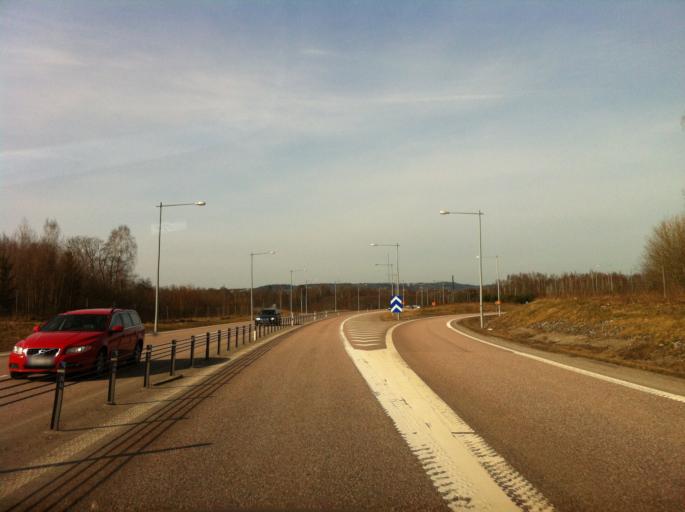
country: SE
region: Vaestra Goetaland
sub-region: Skovde Kommun
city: Skultorp
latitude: 58.3648
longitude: 13.8580
